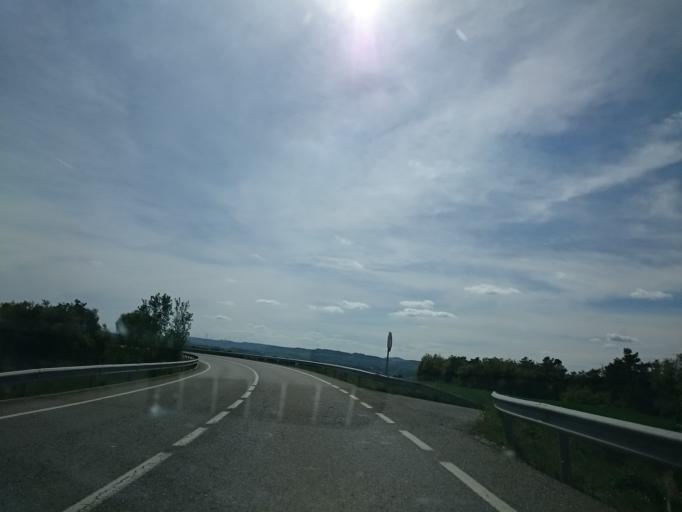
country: ES
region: Catalonia
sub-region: Provincia de Tarragona
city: Santa Coloma de Queralt
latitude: 41.5880
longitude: 1.3922
